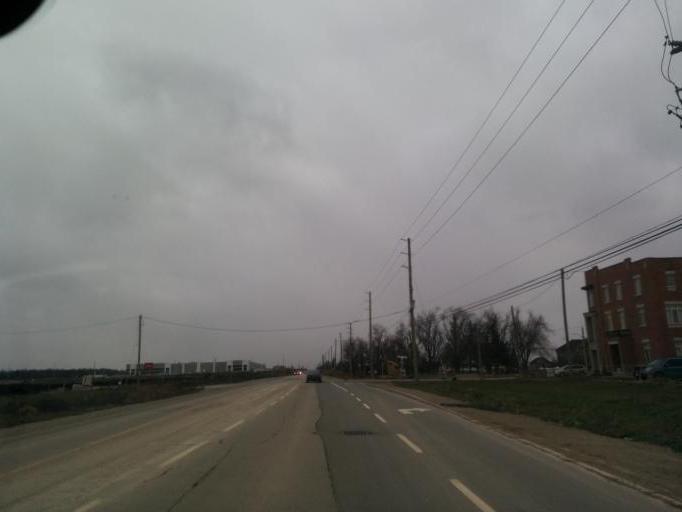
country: CA
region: Ontario
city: Brampton
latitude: 43.7577
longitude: -79.7859
